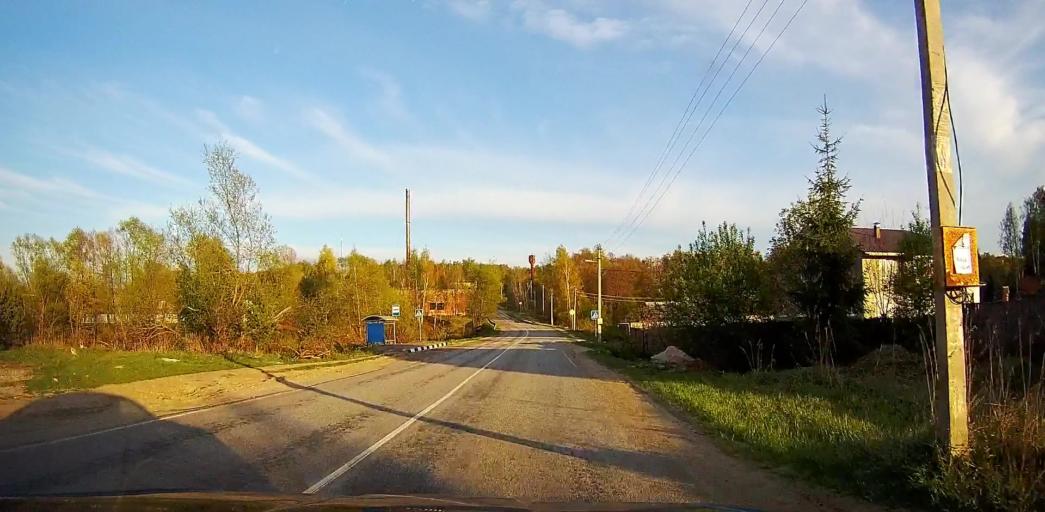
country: RU
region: Moskovskaya
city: Meshcherino
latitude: 55.2307
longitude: 38.3681
